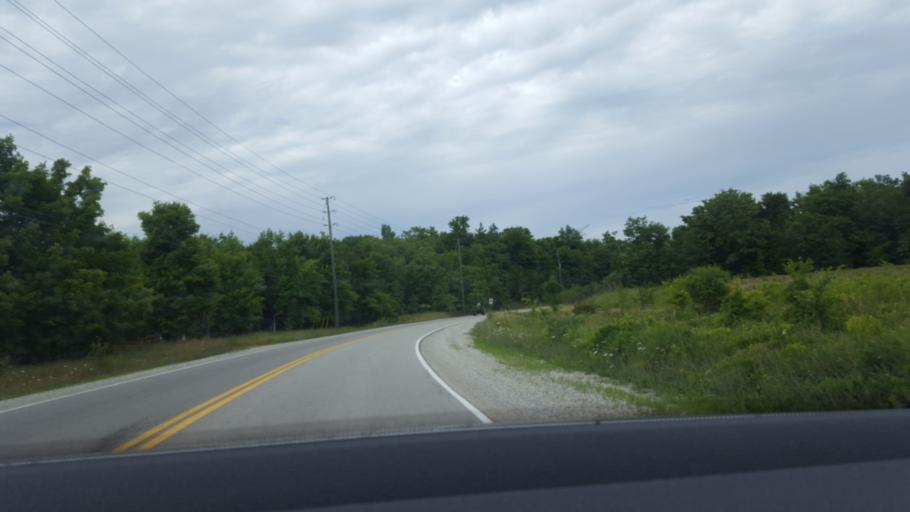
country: CA
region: Ontario
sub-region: Halton
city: Milton
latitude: 43.4973
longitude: -79.9887
